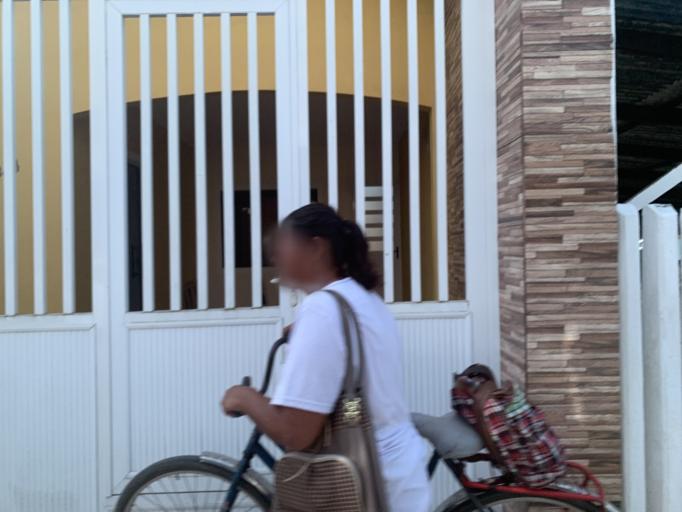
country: BR
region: Parana
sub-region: Antonina
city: Antonina
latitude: -25.4304
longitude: -48.7146
